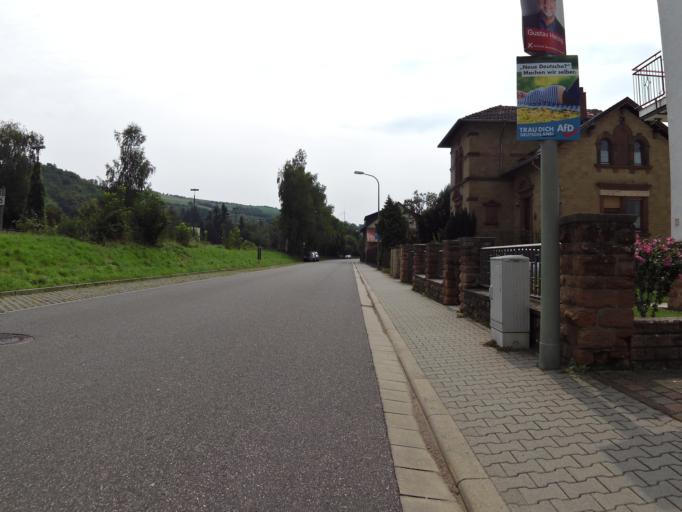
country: DE
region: Rheinland-Pfalz
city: Oberndorf
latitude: 49.7311
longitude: 7.8163
